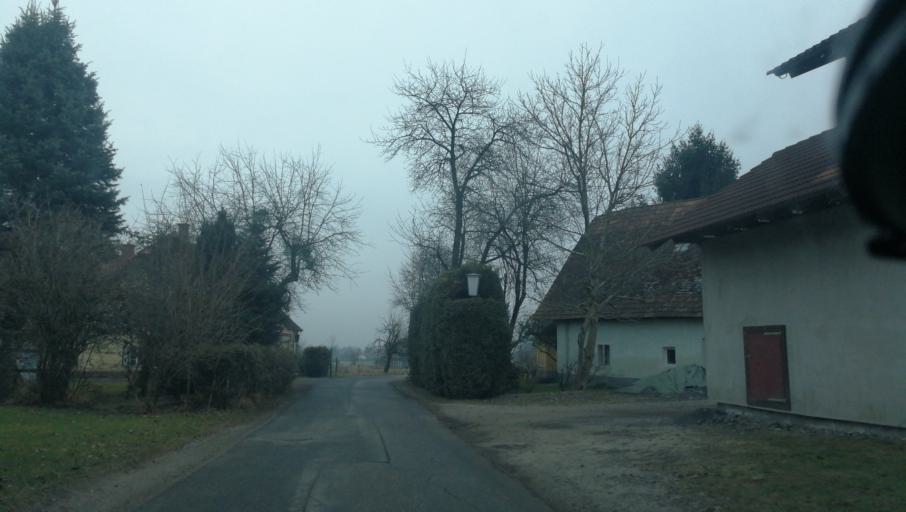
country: AT
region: Styria
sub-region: Politischer Bezirk Deutschlandsberg
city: Stainz
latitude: 46.8947
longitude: 15.2441
